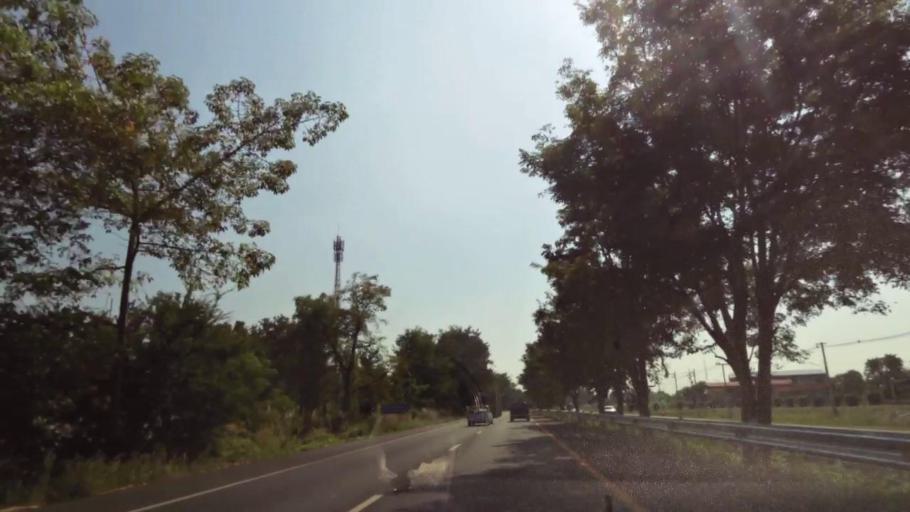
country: TH
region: Nakhon Sawan
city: Kao Liao
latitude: 15.9678
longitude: 100.1197
